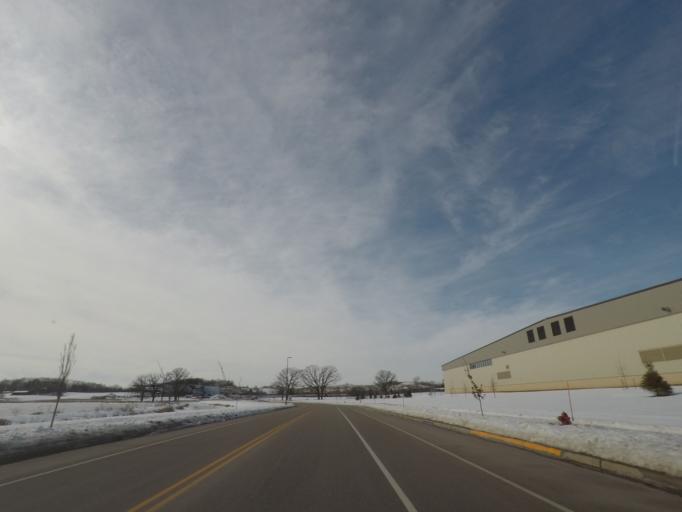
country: US
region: Wisconsin
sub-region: Dane County
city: Fitchburg
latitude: 43.0055
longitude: -89.4627
